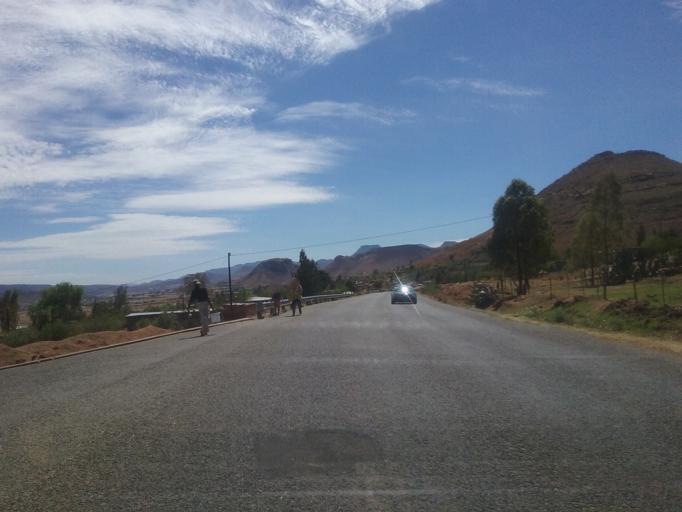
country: LS
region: Mohale's Hoek District
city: Mohale's Hoek
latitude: -30.1877
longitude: 27.4185
